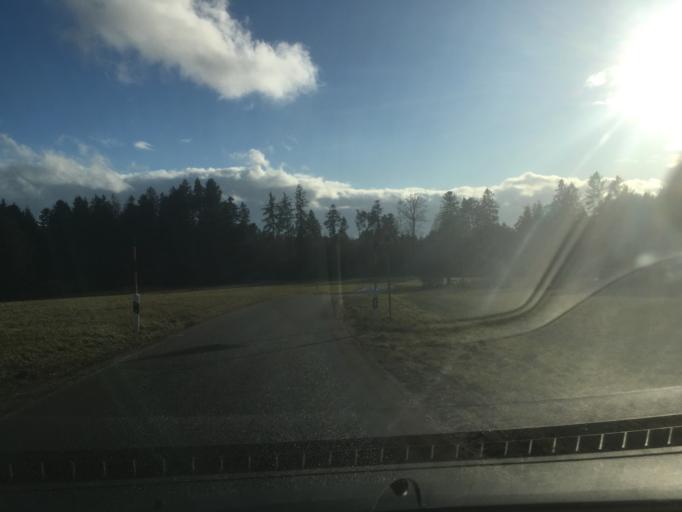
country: DE
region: Baden-Wuerttemberg
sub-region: Freiburg Region
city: Hochenschwand
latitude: 47.6873
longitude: 8.1464
